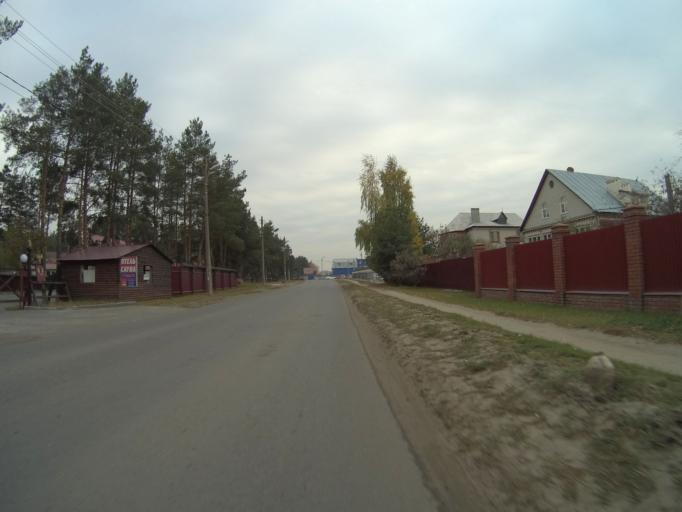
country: RU
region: Vladimir
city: Kommunar
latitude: 56.1162
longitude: 40.4520
